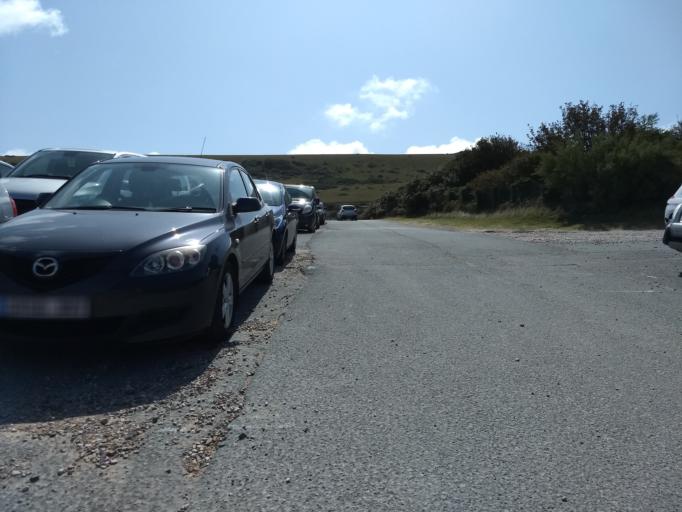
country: GB
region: England
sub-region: Isle of Wight
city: Totland
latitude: 50.6678
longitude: -1.5675
